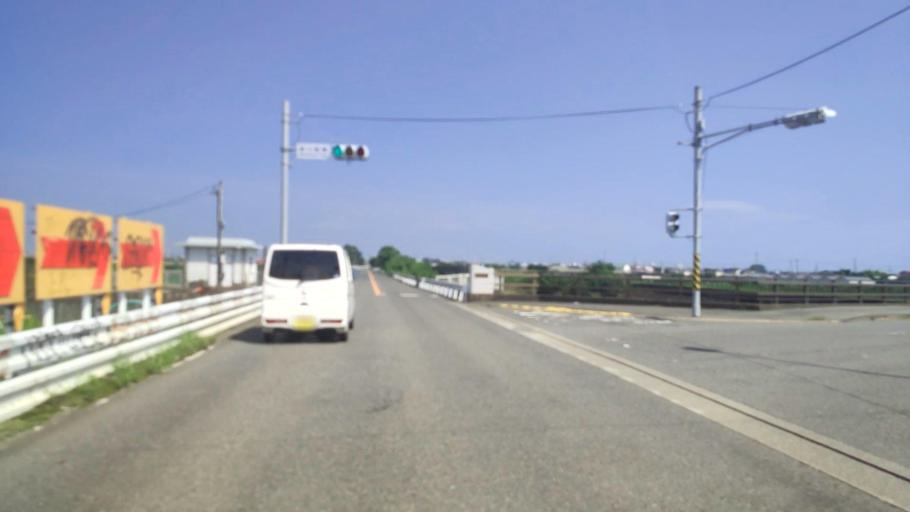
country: JP
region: Kanagawa
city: Isehara
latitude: 35.3671
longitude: 139.3169
